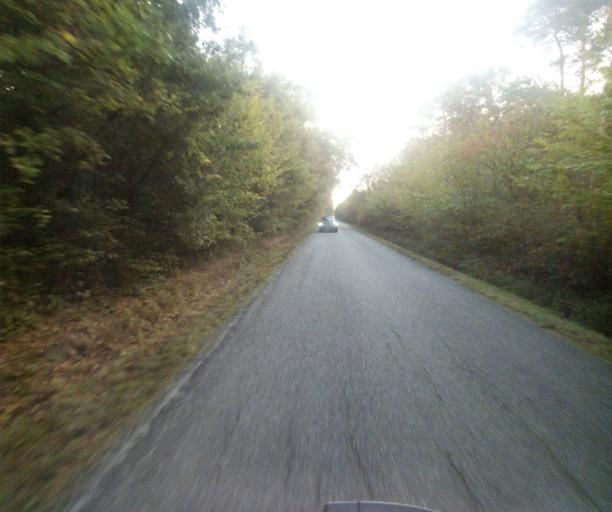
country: FR
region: Midi-Pyrenees
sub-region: Departement du Tarn-et-Garonne
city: Montech
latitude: 43.9420
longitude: 1.2804
